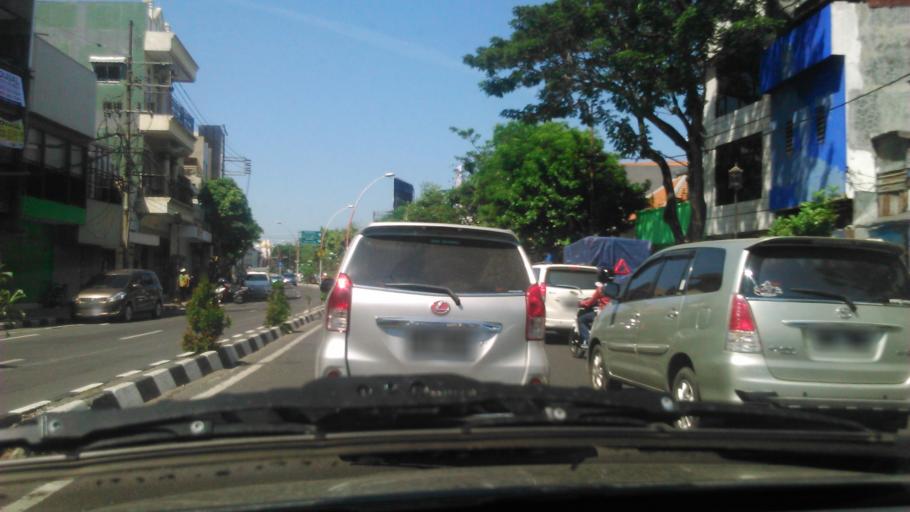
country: ID
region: East Java
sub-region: Kota Surabaya
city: Surabaya
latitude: -7.2559
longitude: 112.7347
